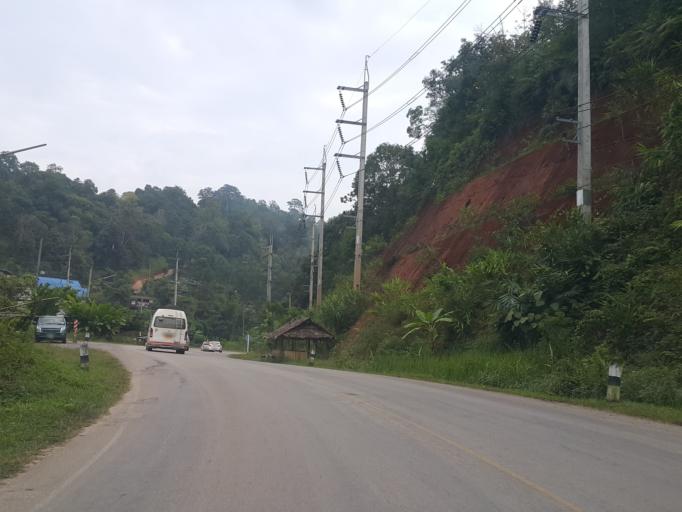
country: TH
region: Chiang Mai
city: Mae Taeng
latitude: 19.1163
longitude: 98.7306
